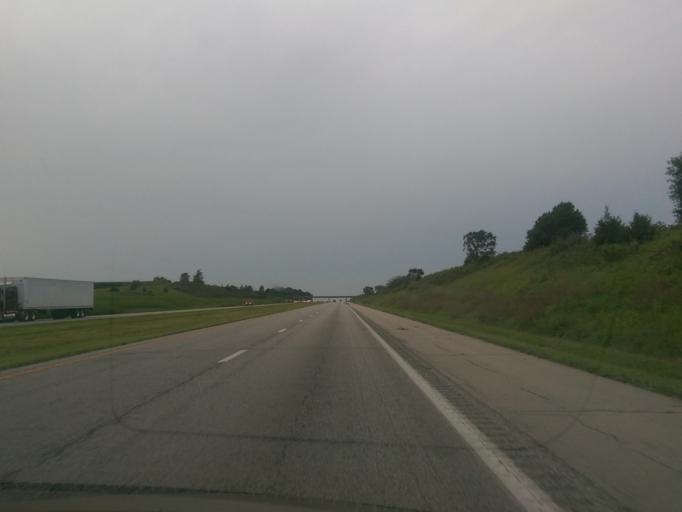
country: US
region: Missouri
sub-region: Holt County
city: Oregon
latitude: 40.0102
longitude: -95.0775
